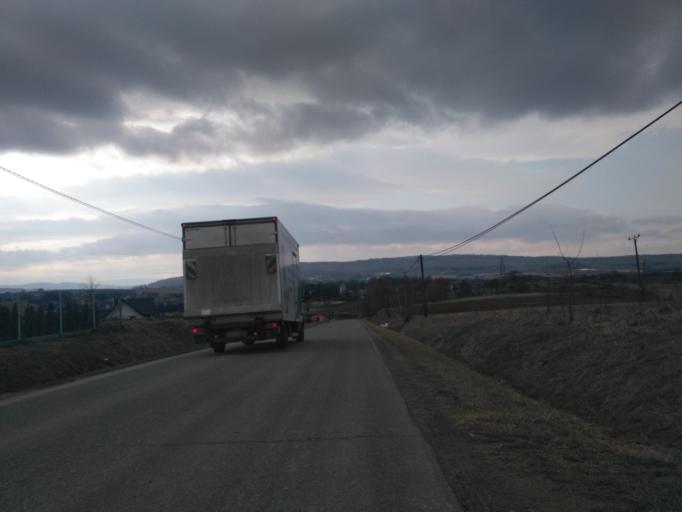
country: PL
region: Subcarpathian Voivodeship
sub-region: Powiat sanocki
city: Strachocina
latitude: 49.6050
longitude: 22.1409
